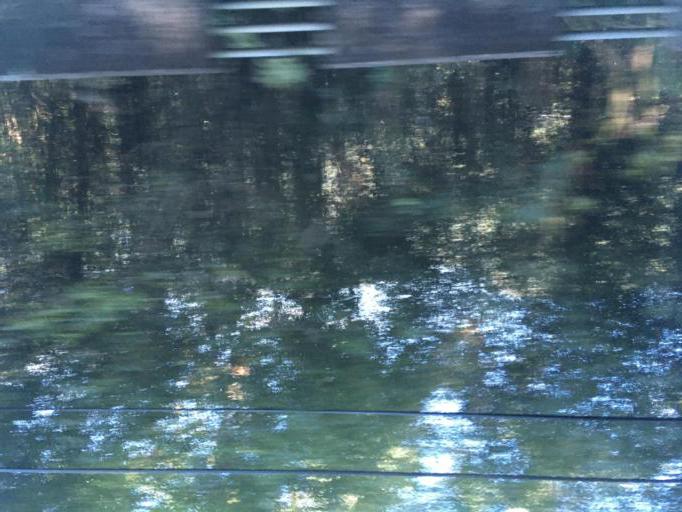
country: TW
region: Taiwan
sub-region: Chiayi
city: Jiayi Shi
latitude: 23.4057
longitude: 120.6549
